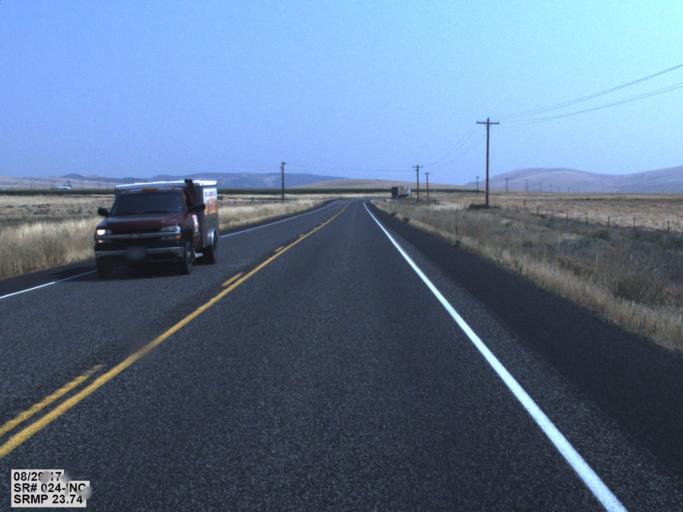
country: US
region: Washington
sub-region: Grant County
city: Desert Aire
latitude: 46.5191
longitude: -120.0159
